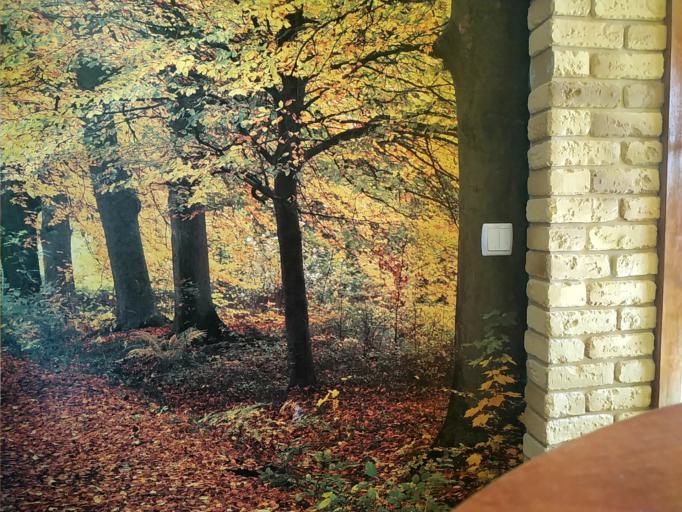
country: RU
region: Jaroslavl
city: Kukoboy
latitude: 58.8503
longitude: 39.7380
